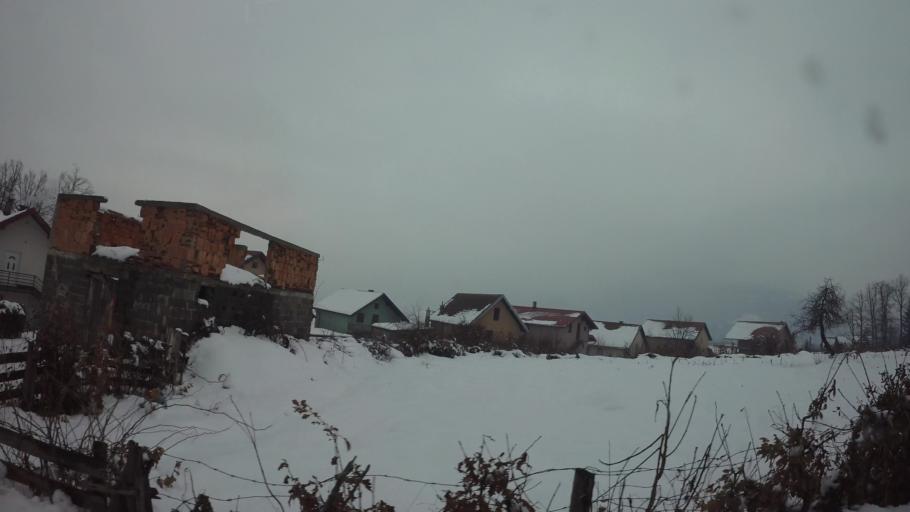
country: BA
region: Federation of Bosnia and Herzegovina
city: Hadzici
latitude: 43.8465
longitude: 18.2717
